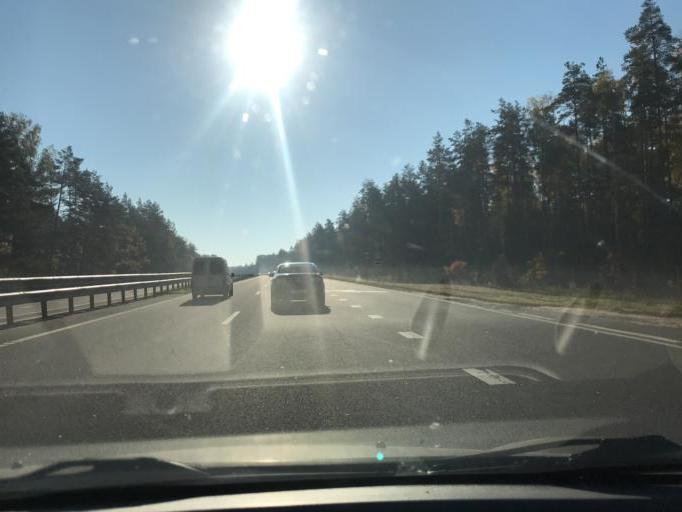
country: BY
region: Minsk
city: Pukhavichy
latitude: 53.4539
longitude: 28.4063
